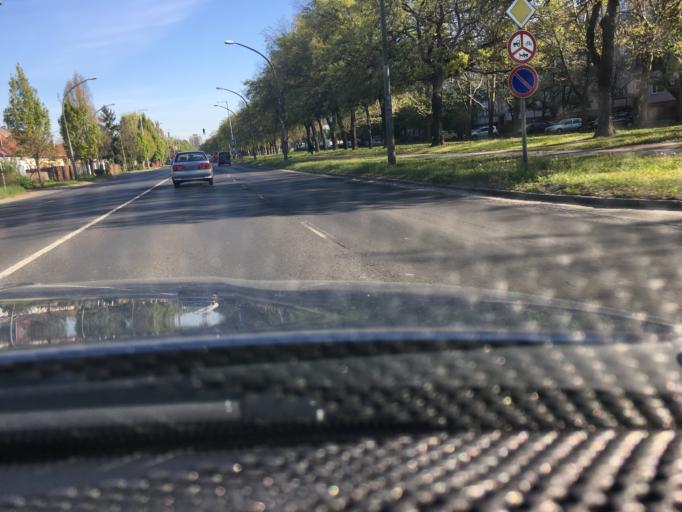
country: HU
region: Hajdu-Bihar
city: Debrecen
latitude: 47.5447
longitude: 21.6097
